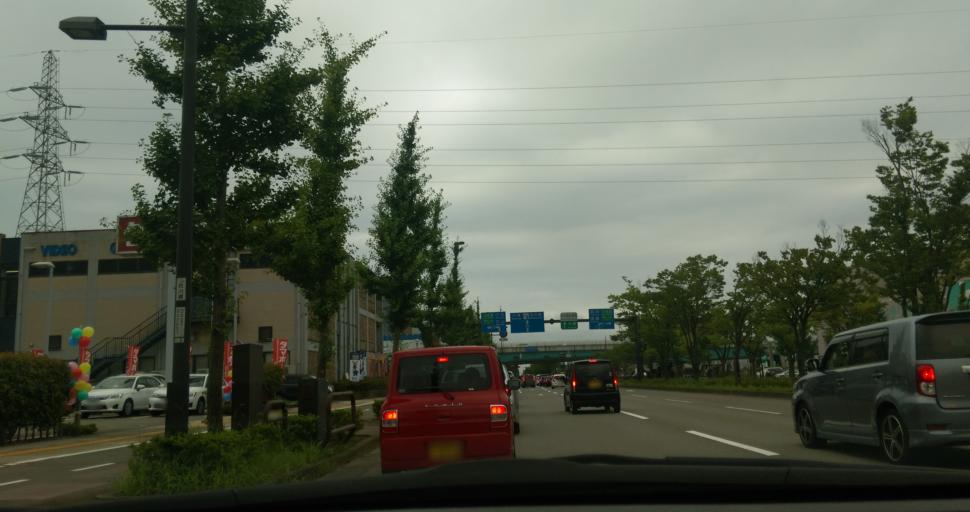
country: JP
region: Ishikawa
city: Kanazawa-shi
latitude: 36.5896
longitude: 136.6322
